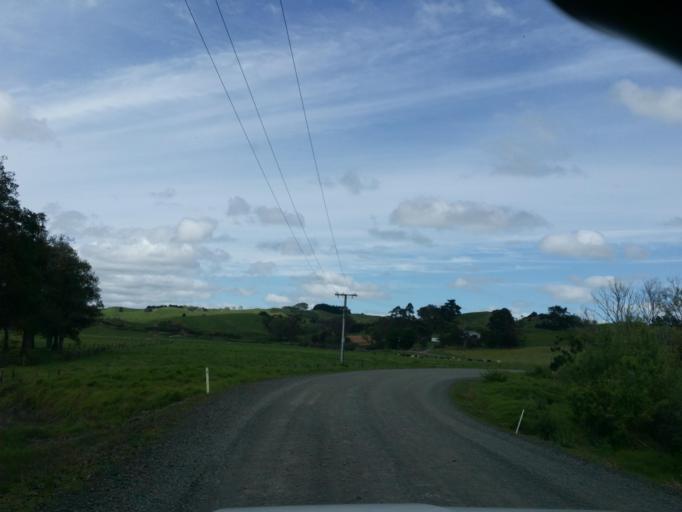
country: NZ
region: Northland
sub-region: Kaipara District
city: Dargaville
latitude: -35.8712
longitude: 174.0355
